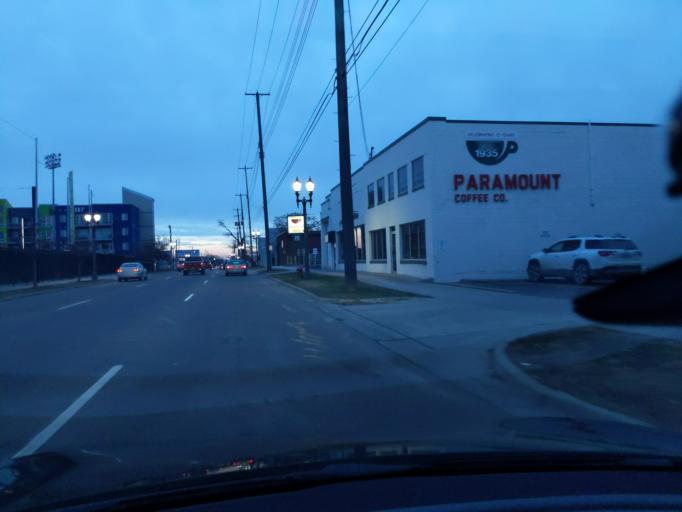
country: US
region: Michigan
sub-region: Ingham County
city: Lansing
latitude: 42.7347
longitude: -84.5446
